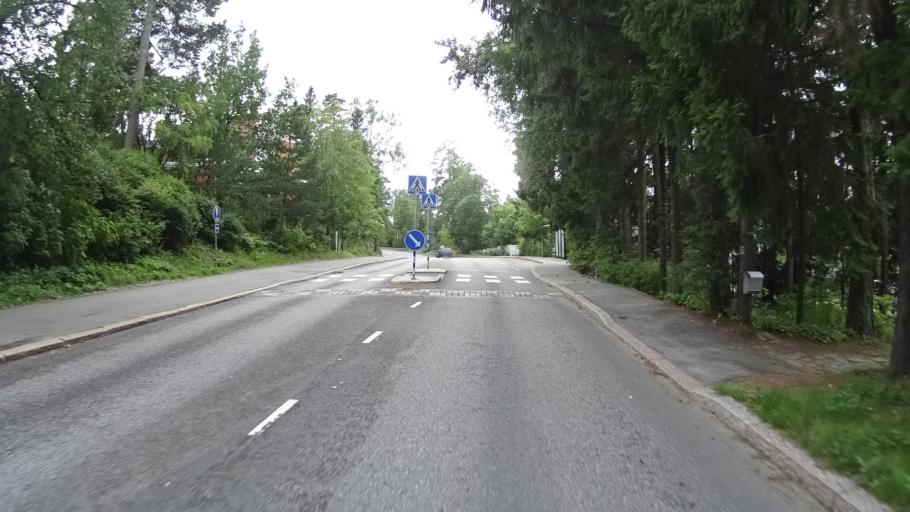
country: FI
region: Uusimaa
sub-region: Helsinki
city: Kauniainen
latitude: 60.2163
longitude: 24.7413
